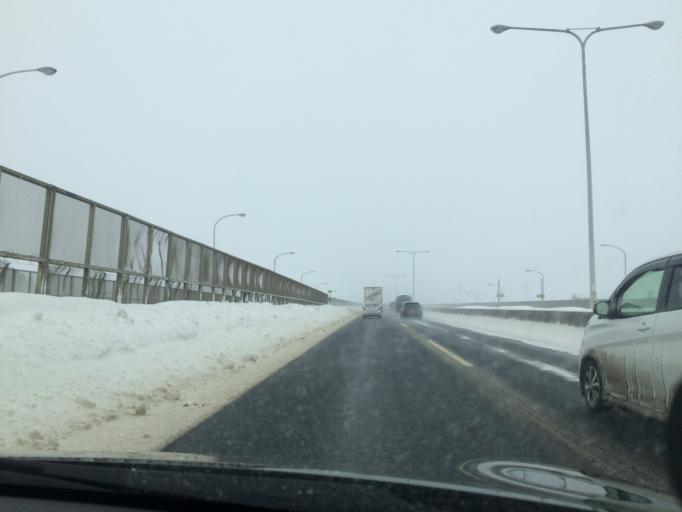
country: JP
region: Hokkaido
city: Sapporo
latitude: 43.0477
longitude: 141.4333
